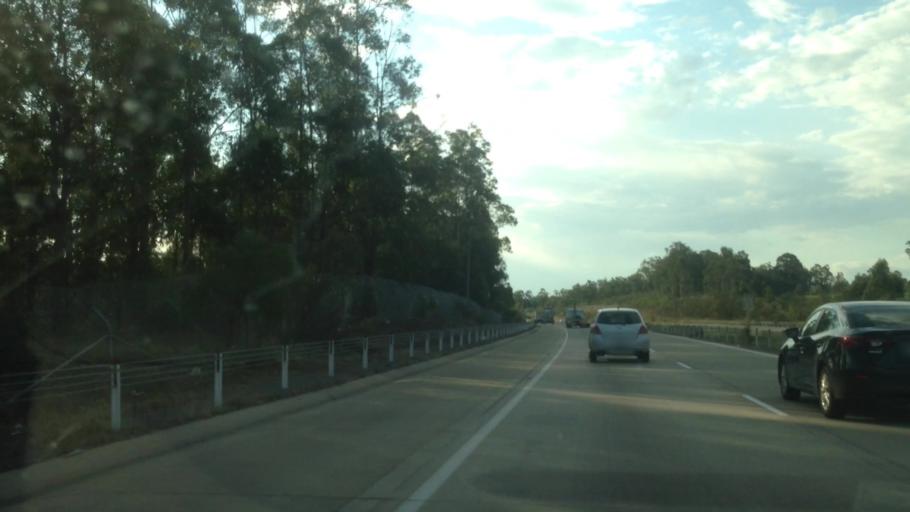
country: AU
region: New South Wales
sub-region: Cessnock
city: Heddon Greta
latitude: -32.8346
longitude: 151.5374
